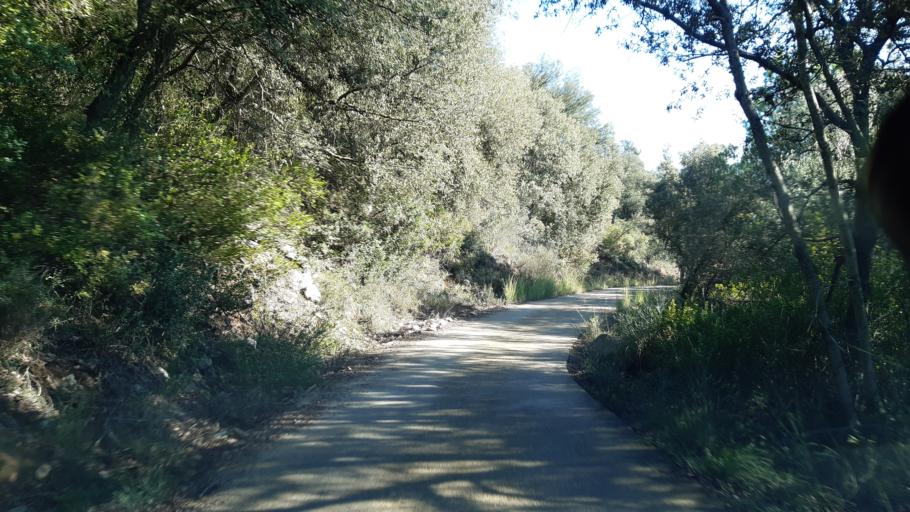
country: ES
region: Catalonia
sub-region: Provincia de Girona
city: la Cellera de Ter
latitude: 42.0191
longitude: 2.6089
